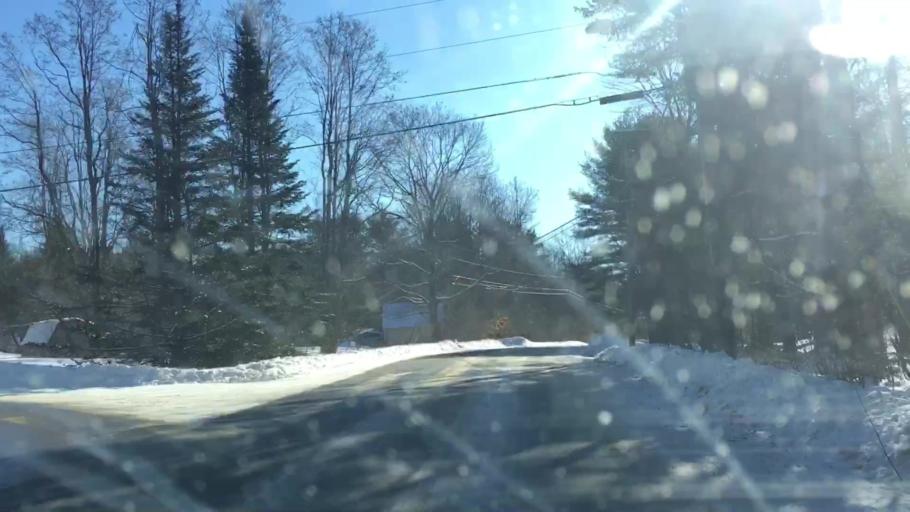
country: US
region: Maine
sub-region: Sagadahoc County
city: Topsham
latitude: 43.8985
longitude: -69.9991
